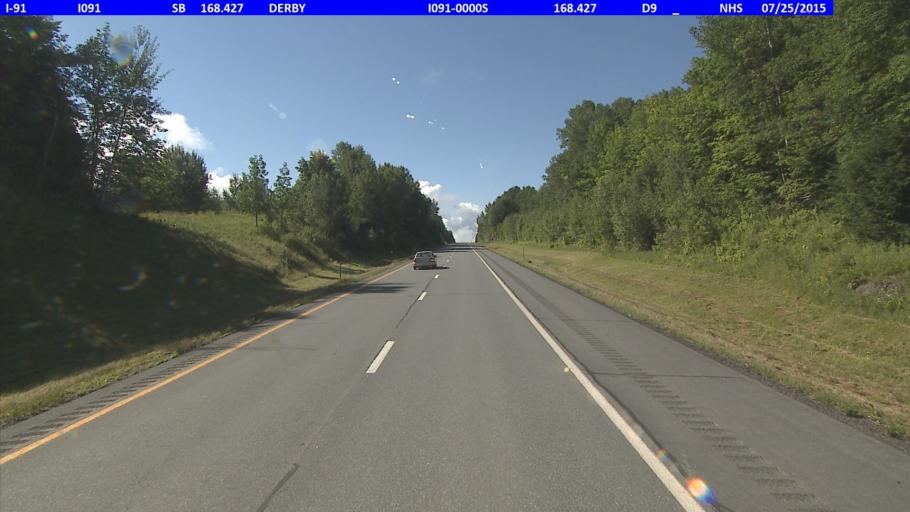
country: US
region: Vermont
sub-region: Orleans County
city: Newport
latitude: 44.9010
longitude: -72.1770
